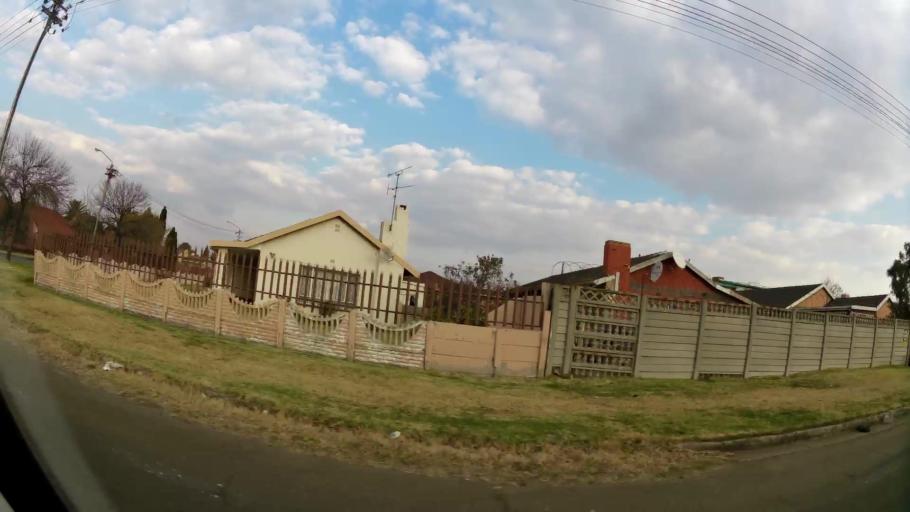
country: ZA
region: Gauteng
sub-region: Ekurhuleni Metropolitan Municipality
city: Germiston
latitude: -26.2498
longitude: 28.1949
